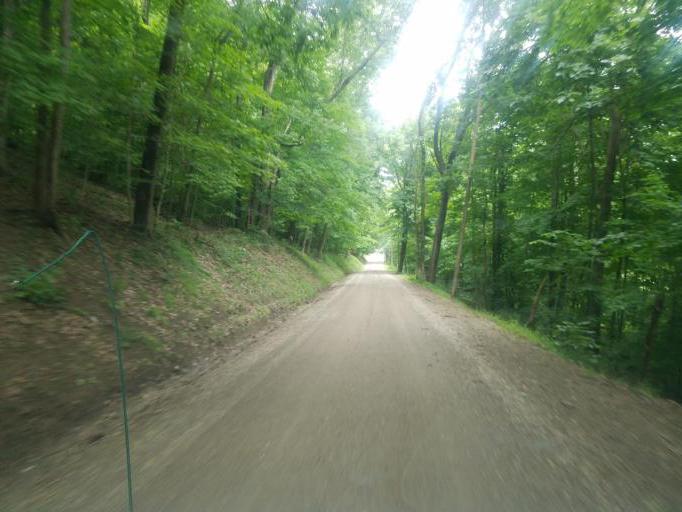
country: US
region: Ohio
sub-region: Knox County
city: Oak Hill
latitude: 40.4028
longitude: -82.1820
